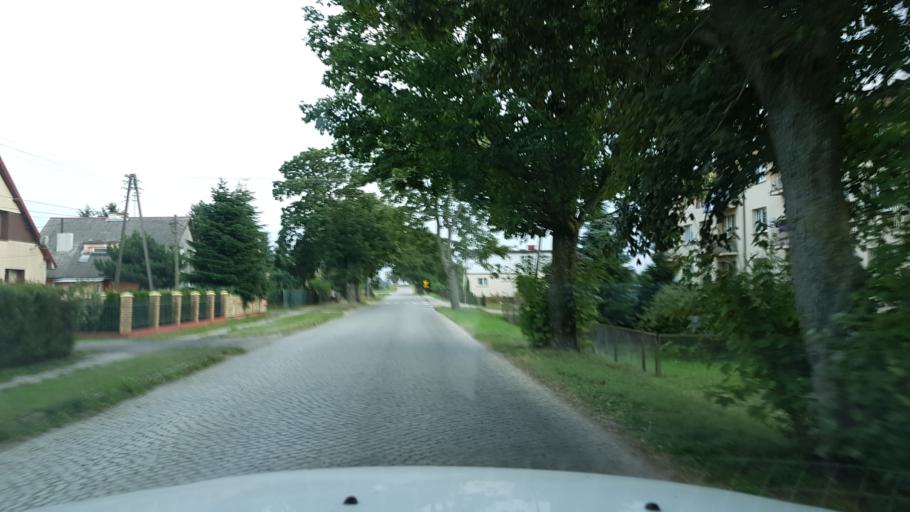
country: PL
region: West Pomeranian Voivodeship
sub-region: Powiat koszalinski
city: Mielno
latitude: 54.2246
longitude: 16.0249
